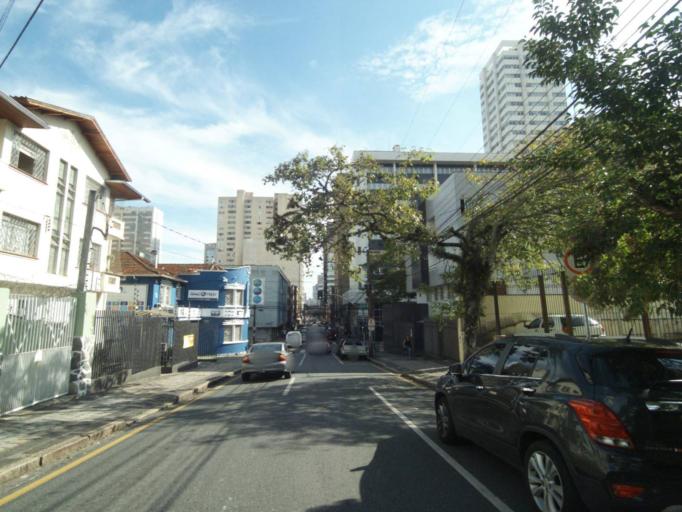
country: BR
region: Parana
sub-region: Curitiba
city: Curitiba
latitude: -25.4280
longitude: -49.2614
